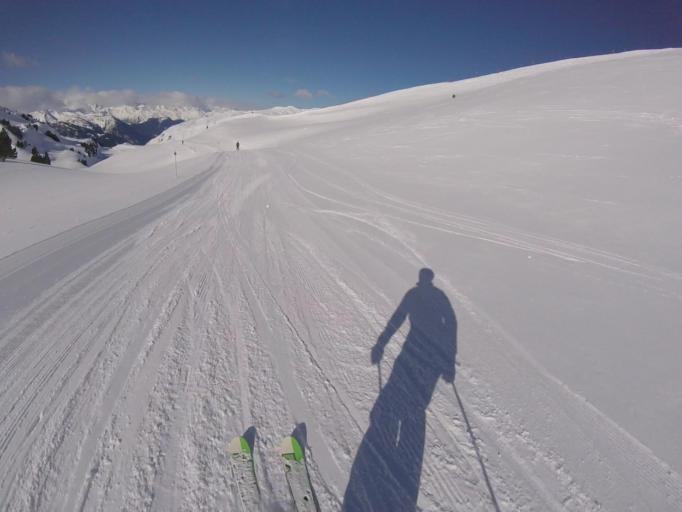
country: ES
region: Catalonia
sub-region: Provincia de Lleida
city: Espot
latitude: 42.7147
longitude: 0.9828
